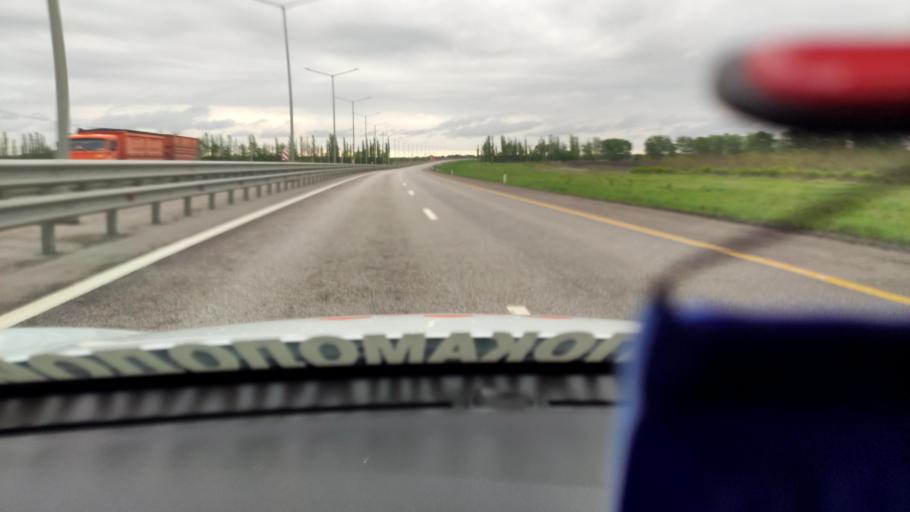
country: RU
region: Voronezj
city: Podkletnoye
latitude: 51.5886
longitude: 39.4348
